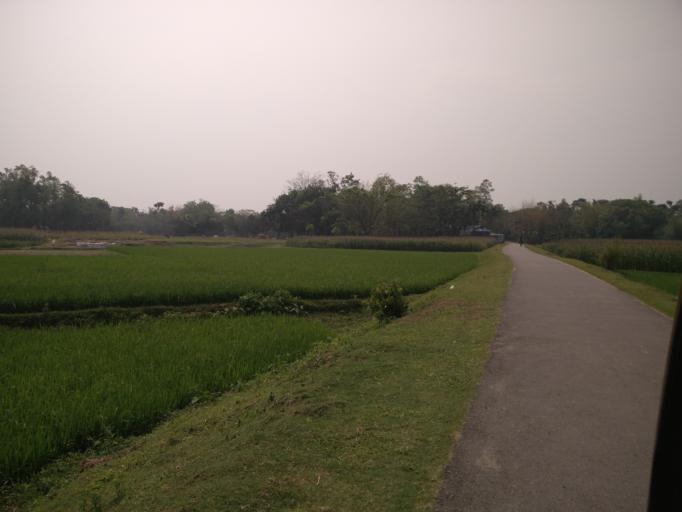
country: BD
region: Dhaka
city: Muktagacha
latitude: 24.9015
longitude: 90.2589
